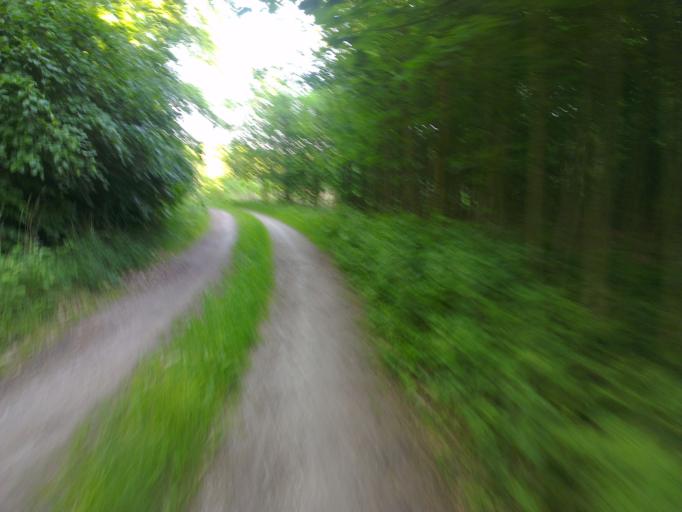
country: DK
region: Capital Region
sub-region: Frederikssund Kommune
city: Jaegerspris
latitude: 55.8747
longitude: 11.9925
